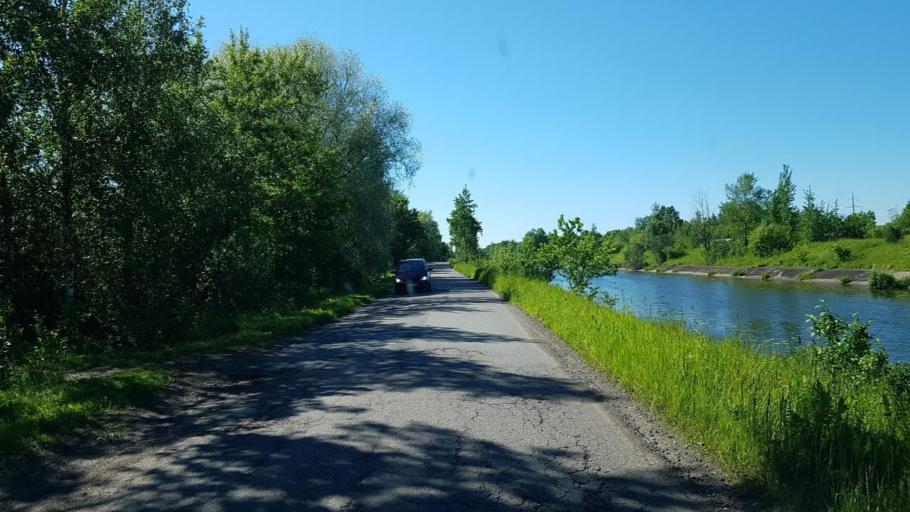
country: EE
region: Ida-Virumaa
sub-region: Narva linn
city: Narva
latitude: 59.3495
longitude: 28.1689
